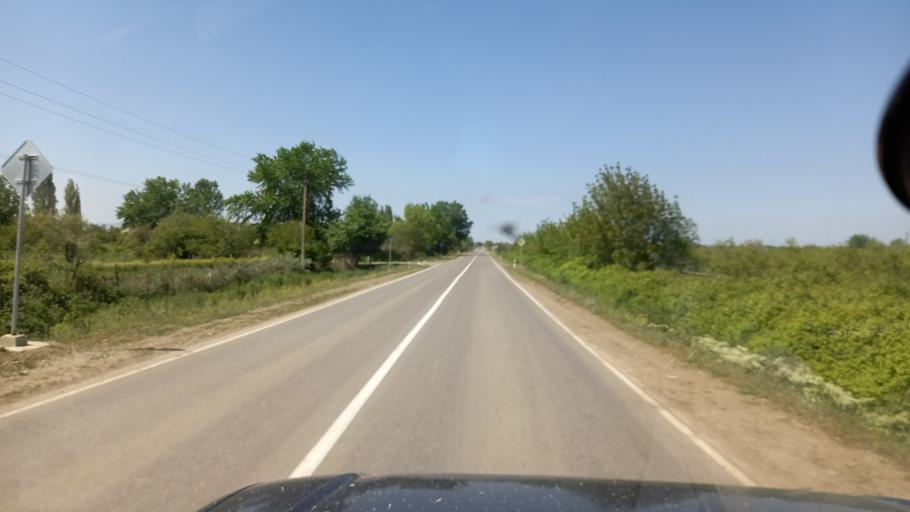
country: RU
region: Dagestan
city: Novaya Maka
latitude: 41.8154
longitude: 48.4032
